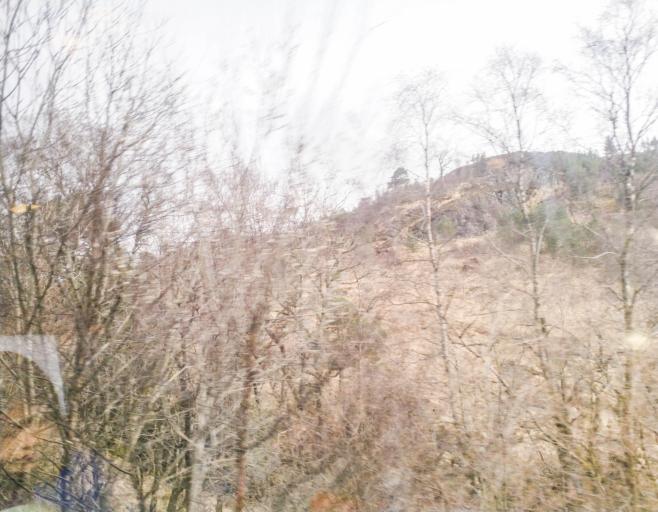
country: GB
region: Scotland
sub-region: Argyll and Bute
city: Garelochhead
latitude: 56.3752
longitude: -4.6482
